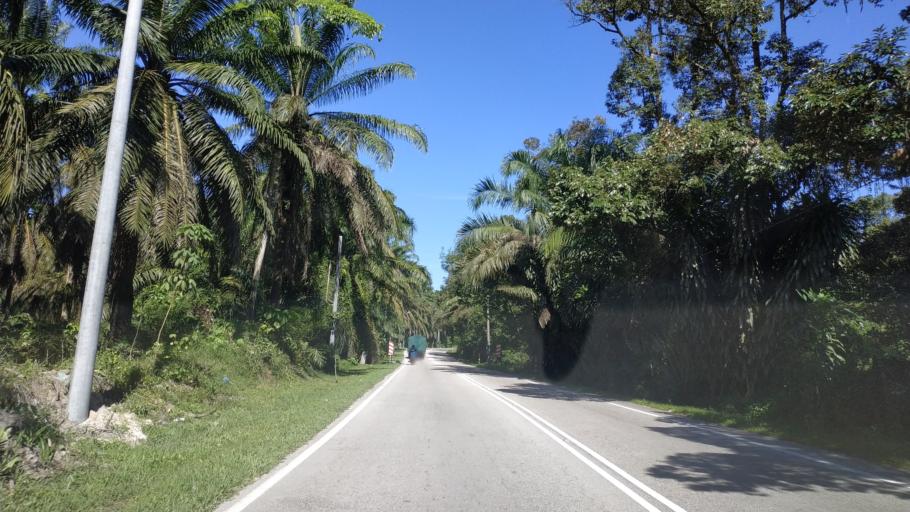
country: MY
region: Kedah
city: Kulim
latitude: 5.3197
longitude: 100.5387
